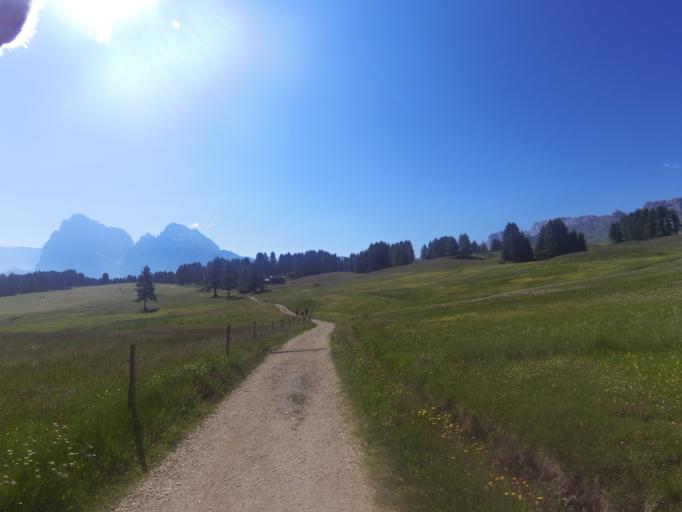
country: IT
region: Trentino-Alto Adige
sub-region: Bolzano
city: Ortisei
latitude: 46.5381
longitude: 11.6408
